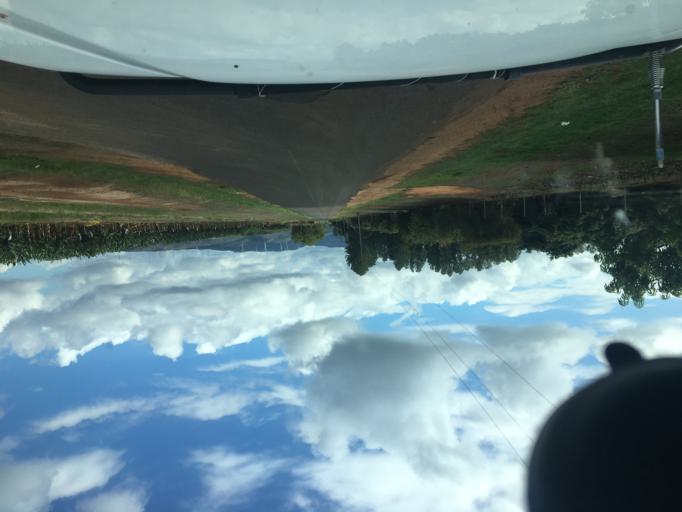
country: AU
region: Queensland
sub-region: Tablelands
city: Mareeba
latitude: -17.1042
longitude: 145.4113
